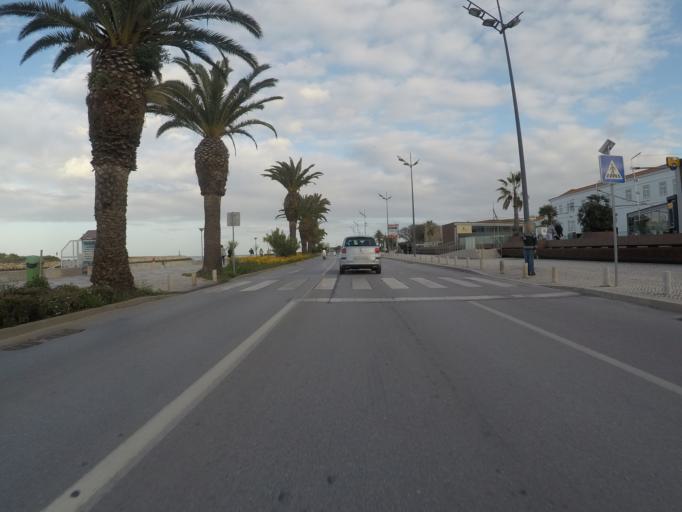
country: PT
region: Faro
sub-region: Lagos
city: Lagos
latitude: 37.1017
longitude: -8.6709
